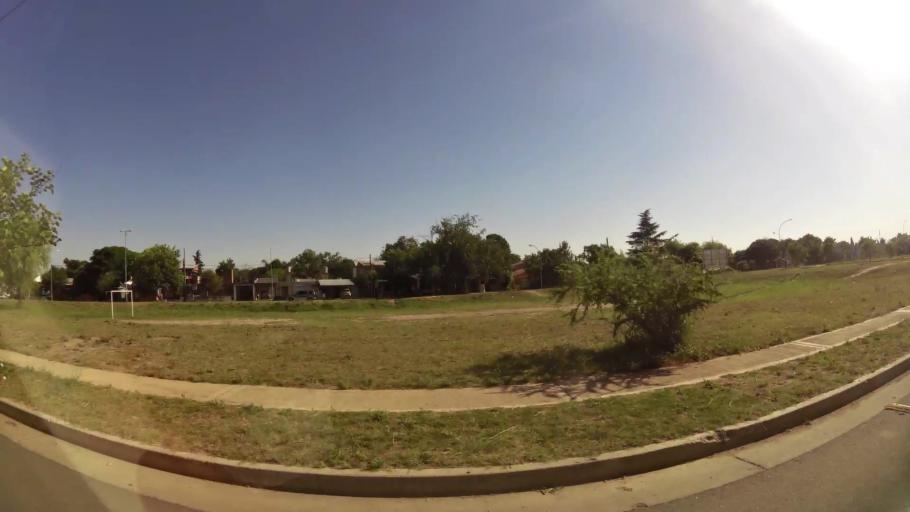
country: AR
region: Cordoba
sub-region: Departamento de Capital
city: Cordoba
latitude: -31.3568
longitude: -64.1906
